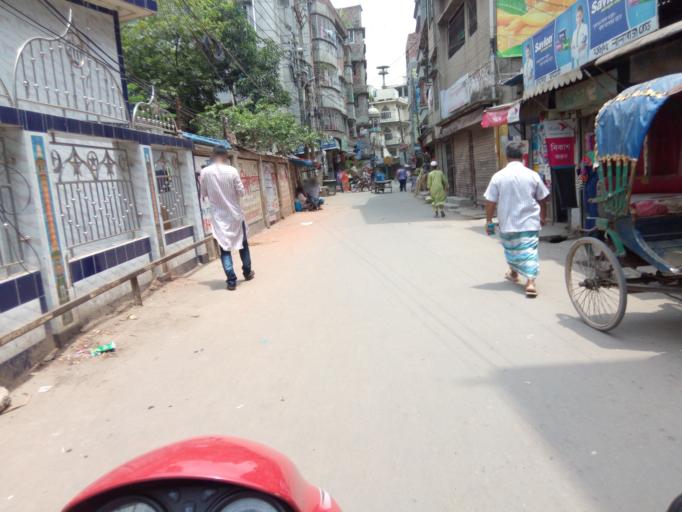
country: BD
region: Dhaka
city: Azimpur
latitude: 23.7249
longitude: 90.3792
